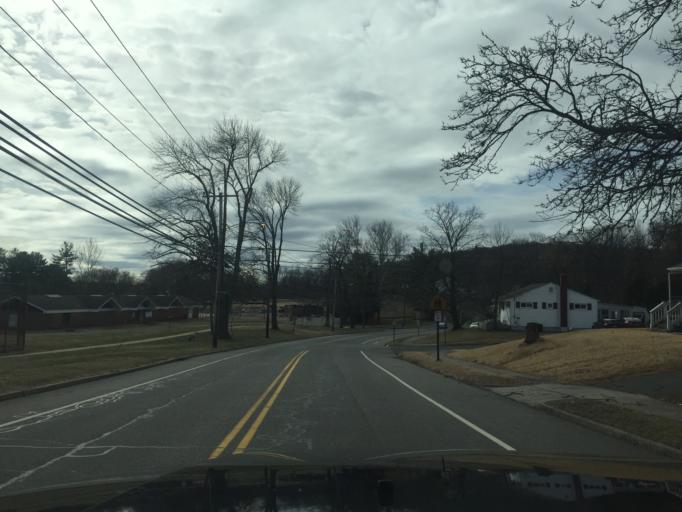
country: US
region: Connecticut
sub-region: Hartford County
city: New Britain
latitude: 41.7073
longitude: -72.7757
